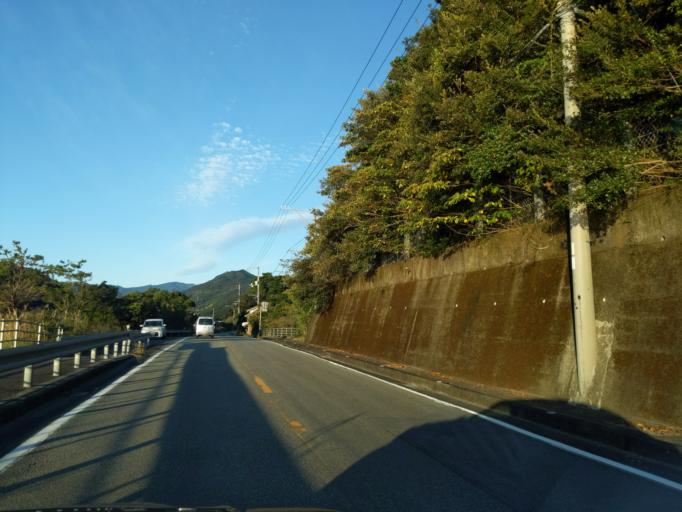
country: JP
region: Kochi
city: Muroto-misakicho
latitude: 33.5856
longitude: 134.3476
